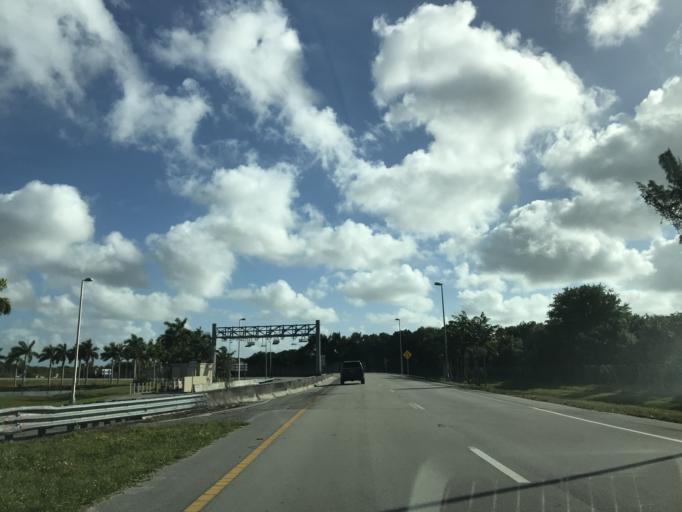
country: US
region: Florida
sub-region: Broward County
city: Parkland
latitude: 26.2980
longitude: -80.2018
